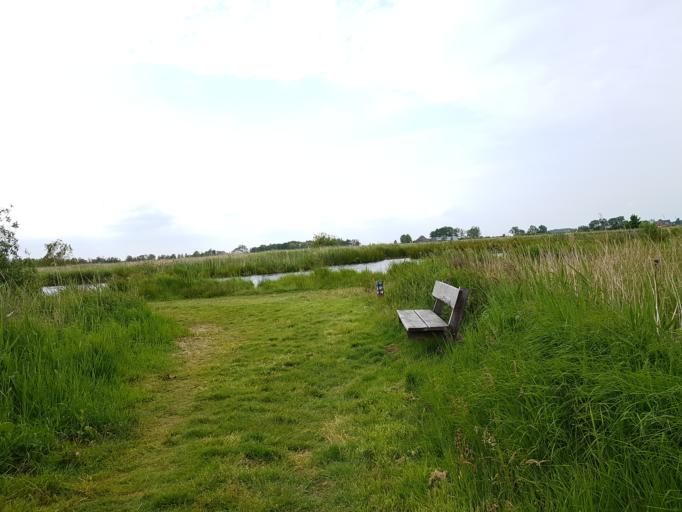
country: NL
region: Friesland
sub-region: Gemeente Tytsjerksteradiel
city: Garyp
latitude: 53.1444
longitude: 5.9424
